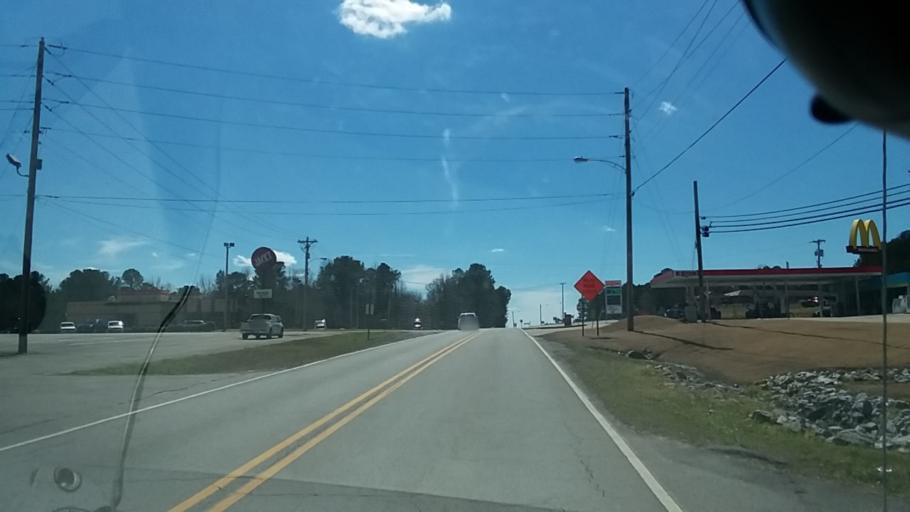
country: US
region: Mississippi
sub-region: Tishomingo County
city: Iuka
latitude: 34.7992
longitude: -88.2057
